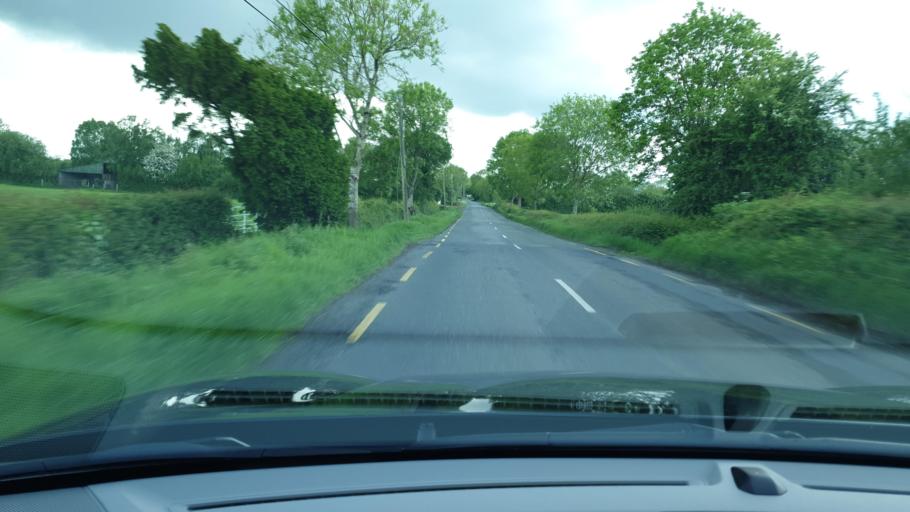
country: IE
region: Leinster
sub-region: Uibh Fhaili
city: Ferbane
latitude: 53.2364
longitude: -7.7222
